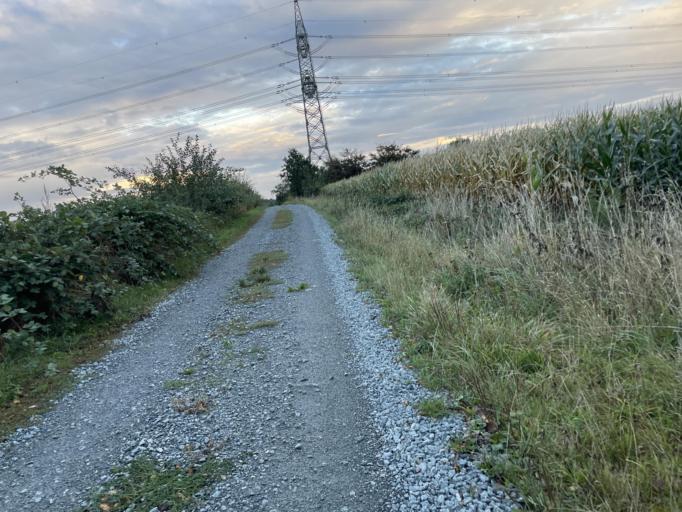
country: DE
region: Schleswig-Holstein
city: Mildstedt
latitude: 54.4776
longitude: 9.1121
